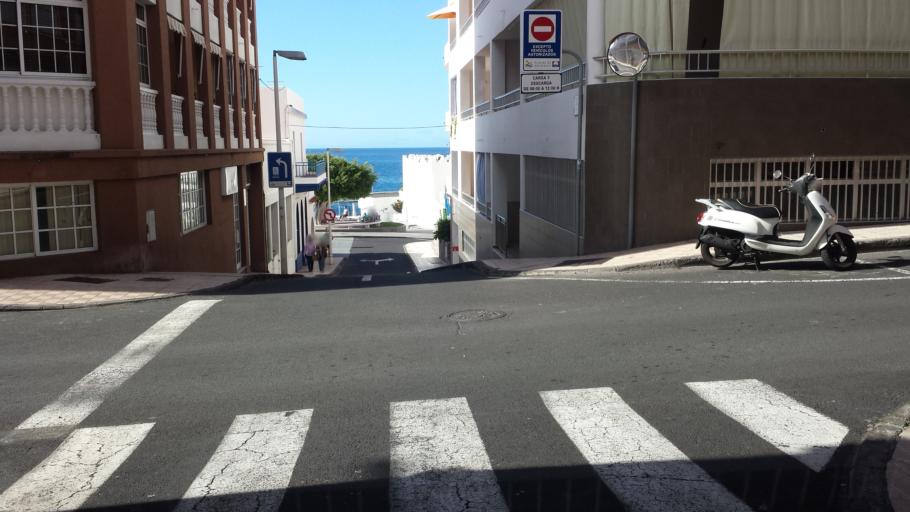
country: ES
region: Canary Islands
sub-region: Provincia de Santa Cruz de Tenerife
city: Tazacorte
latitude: 28.5868
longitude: -17.9098
